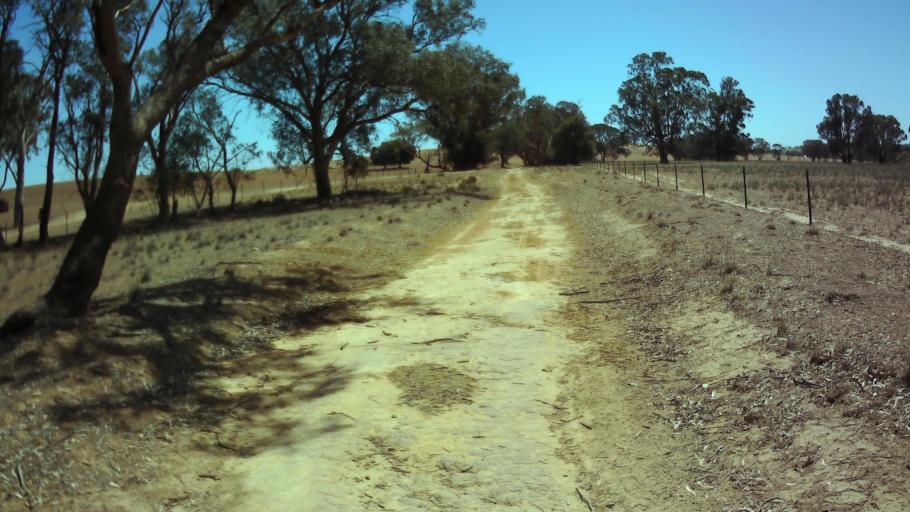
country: AU
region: New South Wales
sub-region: Weddin
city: Grenfell
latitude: -33.9860
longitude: 148.1640
